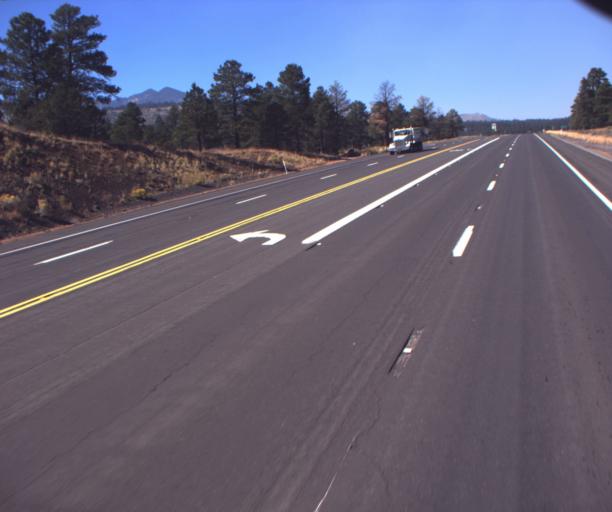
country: US
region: Arizona
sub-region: Coconino County
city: Flagstaff
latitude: 35.3399
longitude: -111.5566
